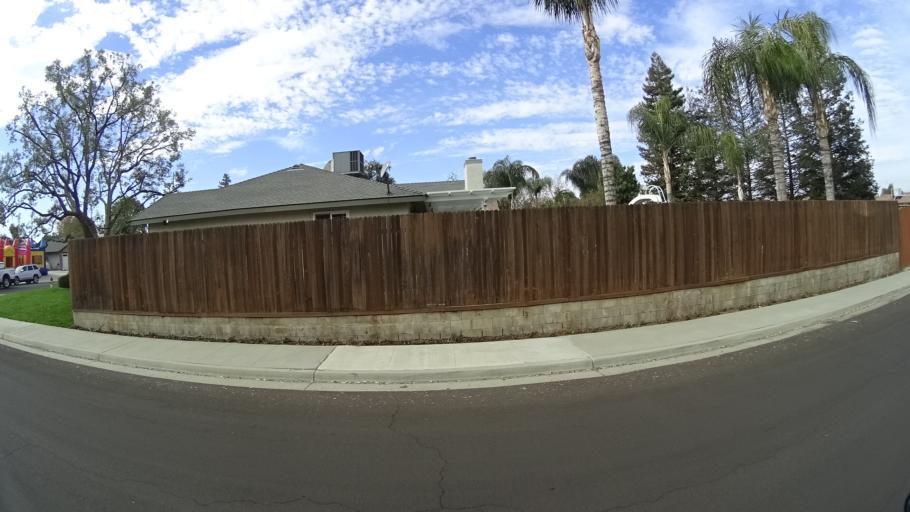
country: US
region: California
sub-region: Kern County
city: Greenacres
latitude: 35.3940
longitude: -119.1262
